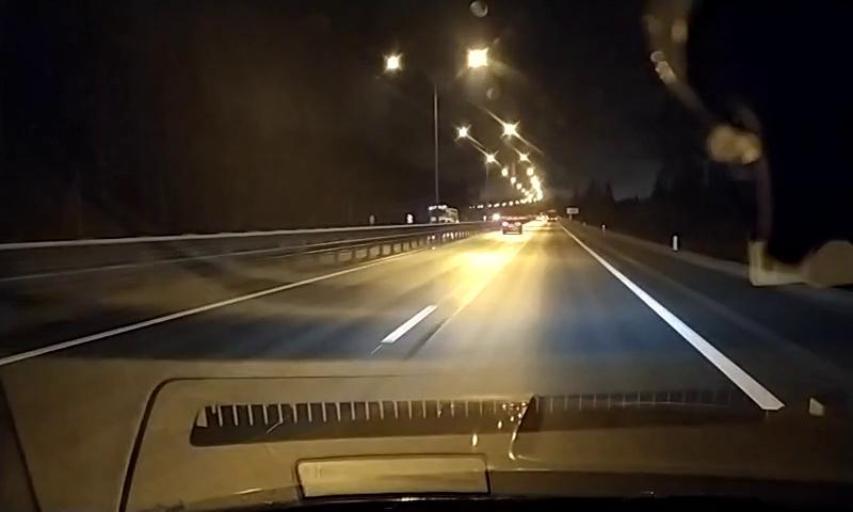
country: RU
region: Leningrad
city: Luppolovo
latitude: 60.1519
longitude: 30.3576
